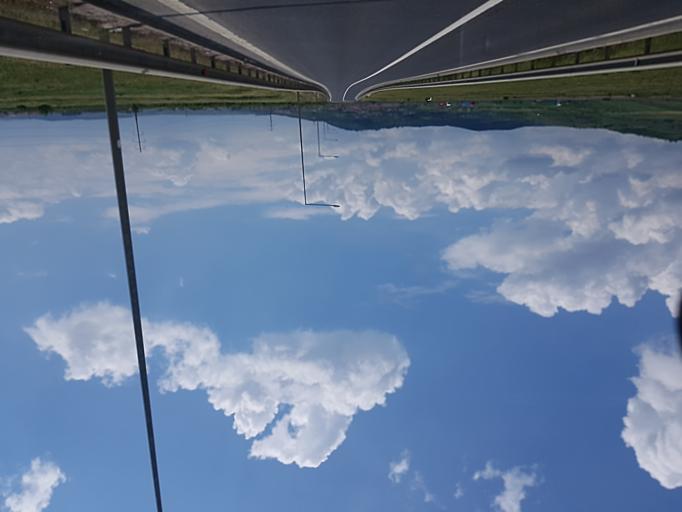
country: RO
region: Sibiu
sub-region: Municipiul Sibiu
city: Sibiu
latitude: 45.8208
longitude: 24.1545
